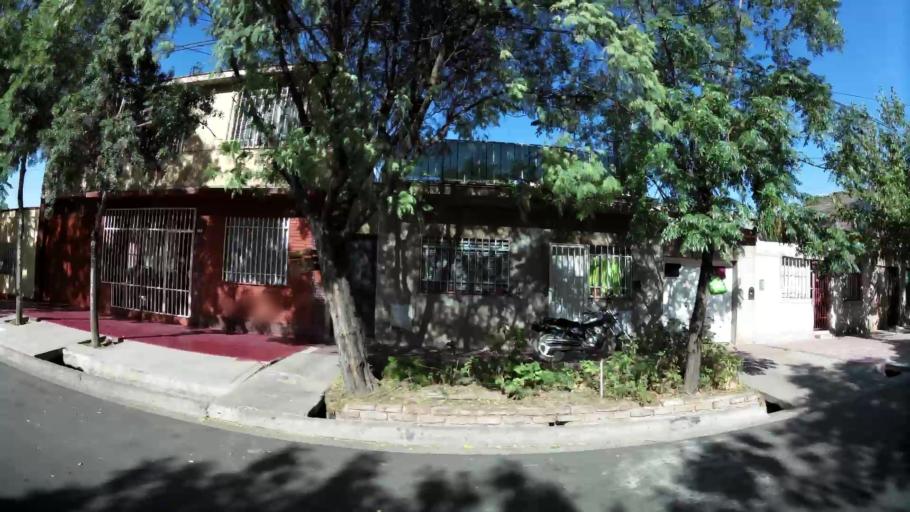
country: AR
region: Mendoza
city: Mendoza
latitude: -32.9002
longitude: -68.8180
